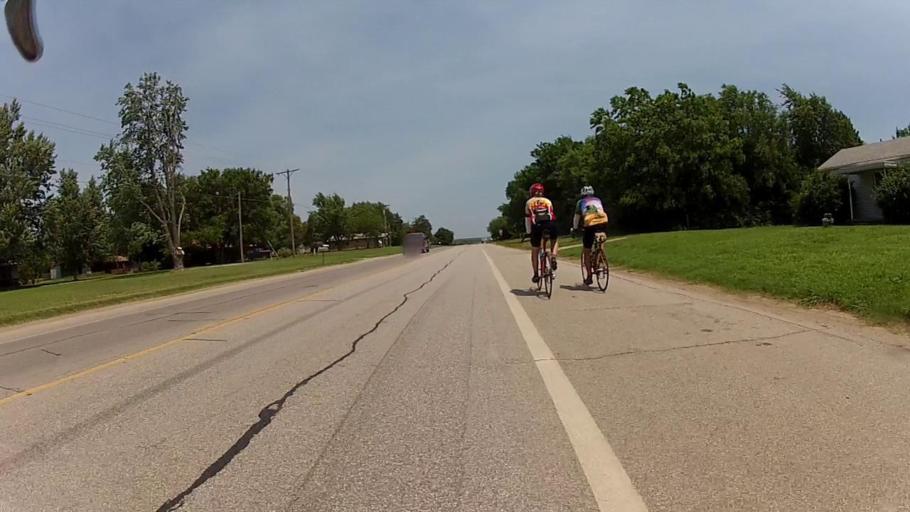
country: US
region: Kansas
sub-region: Cowley County
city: Arkansas City
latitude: 37.0565
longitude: -97.0795
